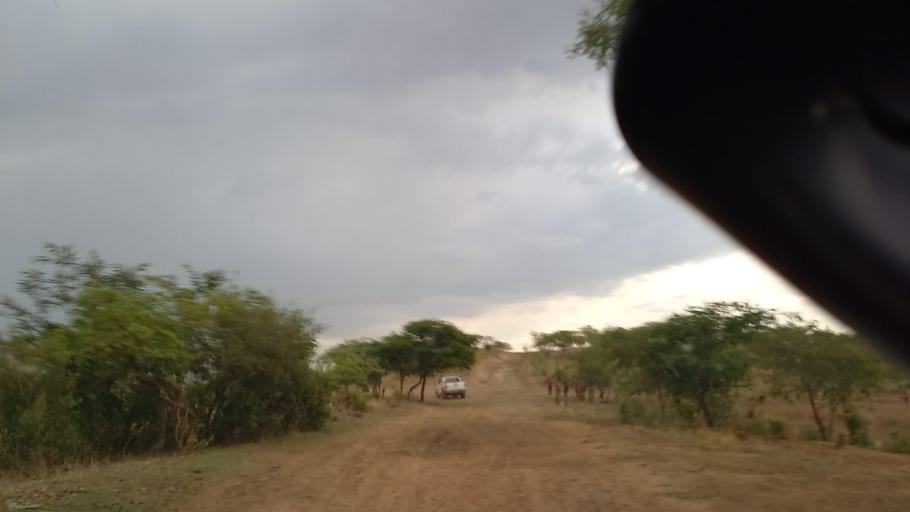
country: ZM
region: Lusaka
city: Kafue
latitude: -16.1245
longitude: 28.0616
